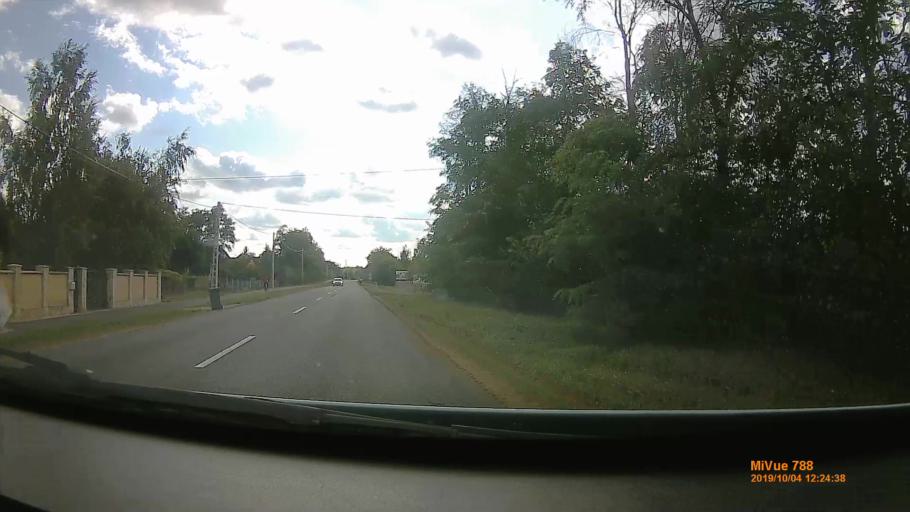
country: HU
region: Szabolcs-Szatmar-Bereg
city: Nyiregyhaza
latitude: 47.9943
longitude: 21.7031
